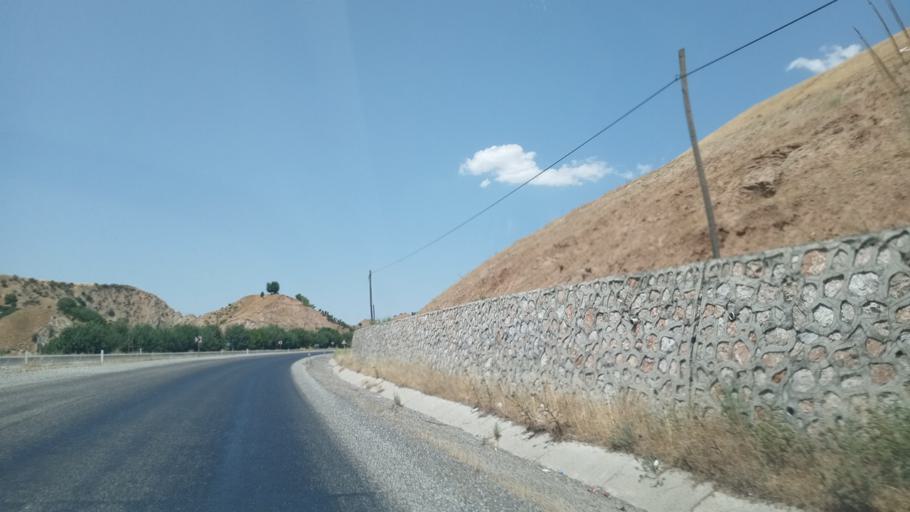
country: TR
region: Batman
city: Kozluk
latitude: 38.1696
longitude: 41.4559
